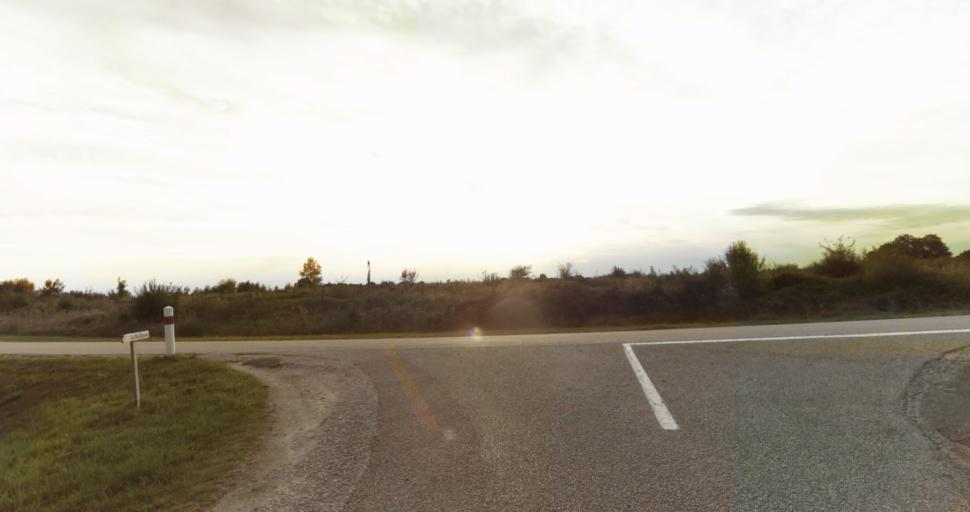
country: FR
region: Lower Normandy
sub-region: Departement de l'Orne
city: Gace
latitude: 48.7417
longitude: 0.2719
